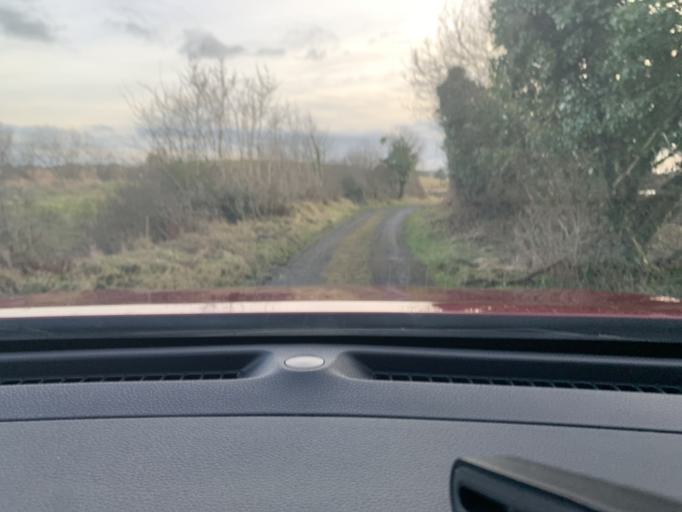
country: IE
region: Connaught
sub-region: Sligo
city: Strandhill
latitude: 54.1705
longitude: -8.6477
